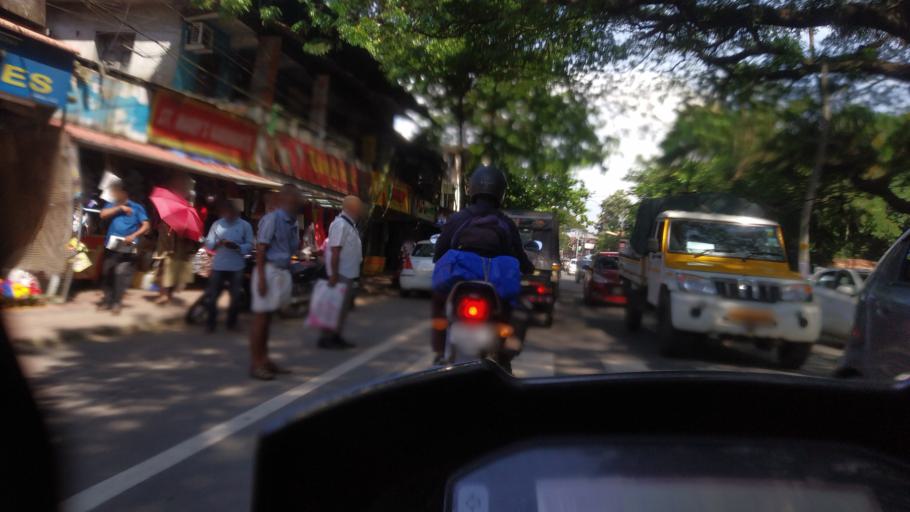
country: IN
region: Kerala
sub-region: Thrissur District
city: Kodungallur
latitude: 10.1490
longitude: 76.2309
